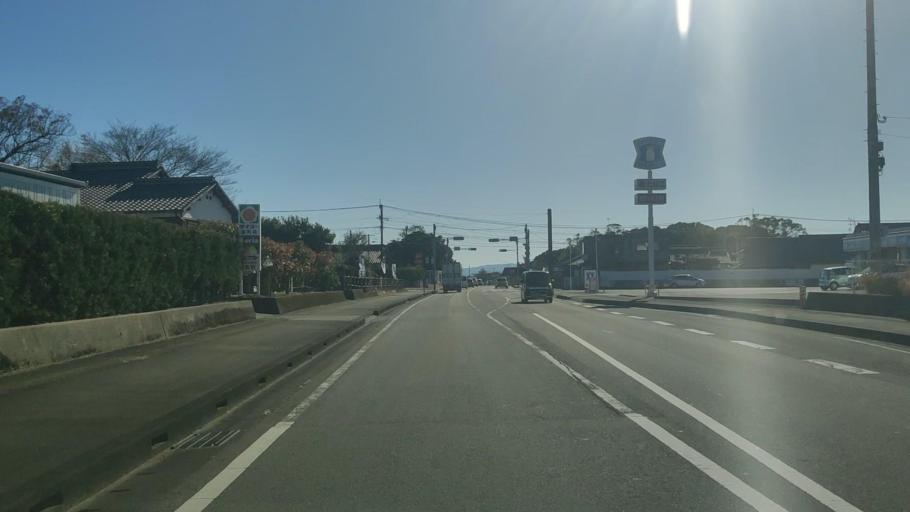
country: JP
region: Miyazaki
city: Miyazaki-shi
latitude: 31.9523
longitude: 131.4604
